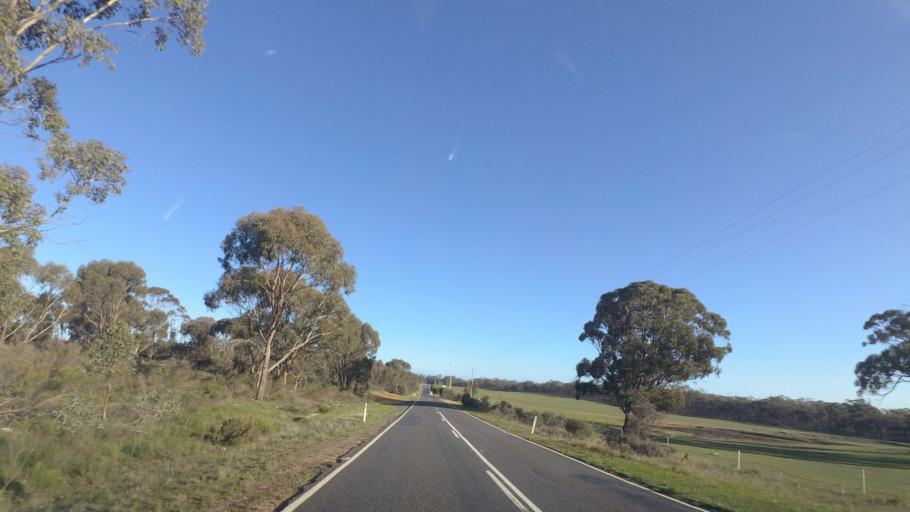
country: AU
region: Victoria
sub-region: Greater Bendigo
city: Kennington
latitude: -36.8665
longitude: 144.5009
